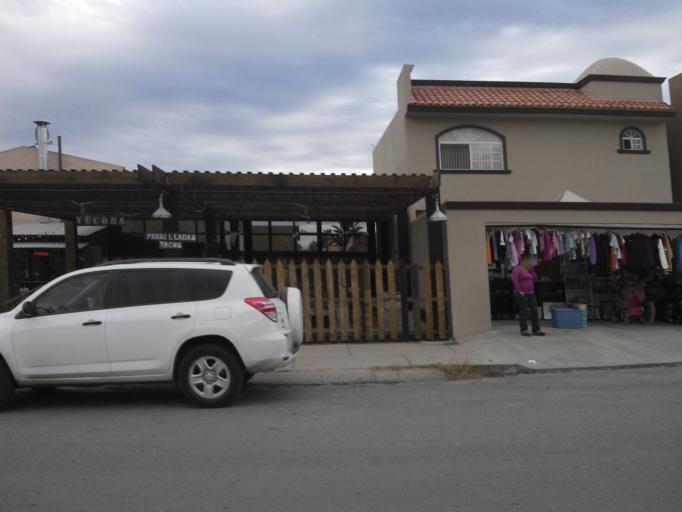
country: US
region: California
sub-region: San Diego County
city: Imperial Beach
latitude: 32.5276
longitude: -117.1219
